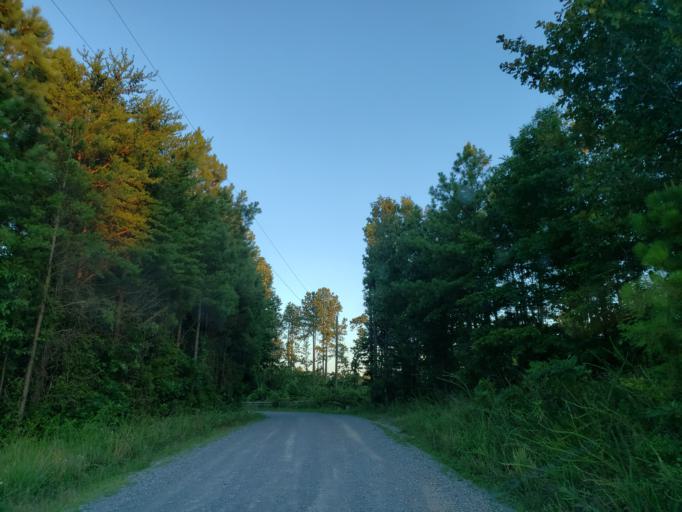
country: US
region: Georgia
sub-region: Bartow County
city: Euharlee
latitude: 34.0604
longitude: -84.8542
